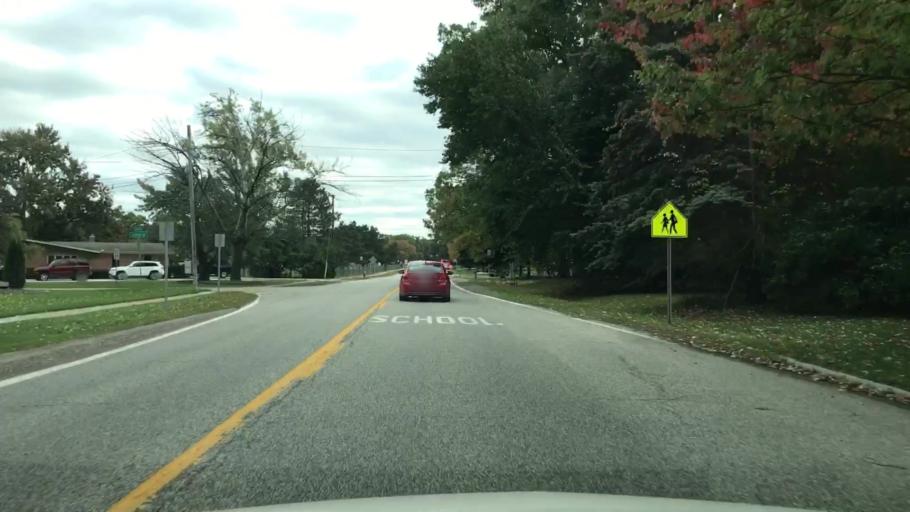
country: US
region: Michigan
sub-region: Macomb County
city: Shelby
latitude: 42.6875
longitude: -83.0691
